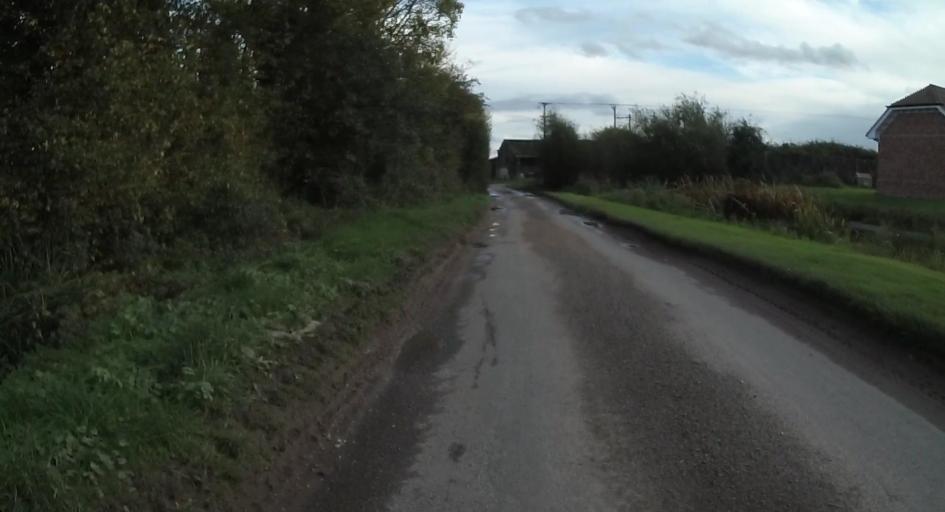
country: GB
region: England
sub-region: Wokingham
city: Swallowfield
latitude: 51.3707
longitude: -0.9588
